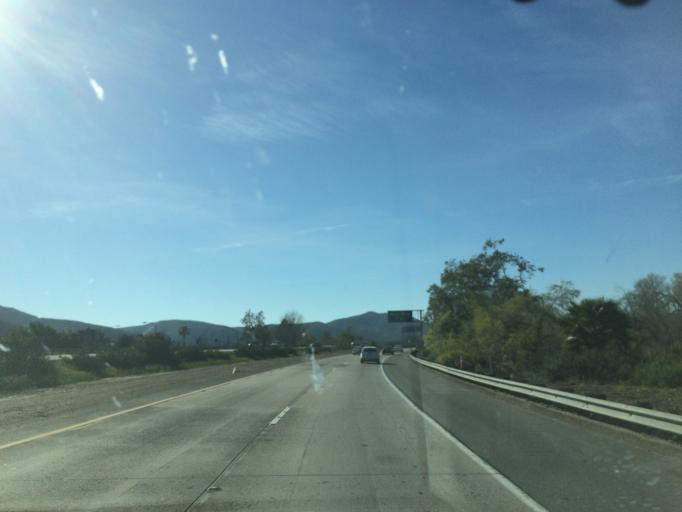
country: US
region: California
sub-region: San Diego County
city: Santee
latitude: 32.8363
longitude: -117.0172
